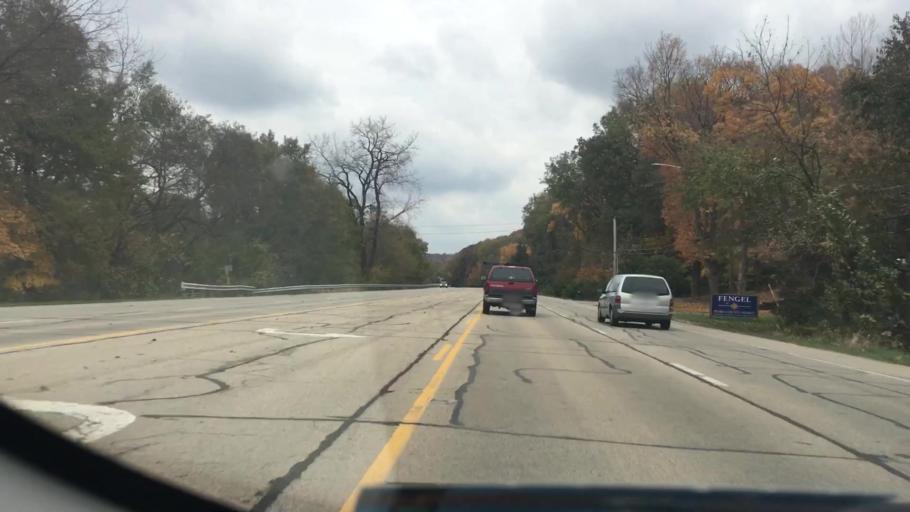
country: US
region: Illinois
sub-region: Peoria County
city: Peoria Heights
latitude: 40.7834
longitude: -89.5774
